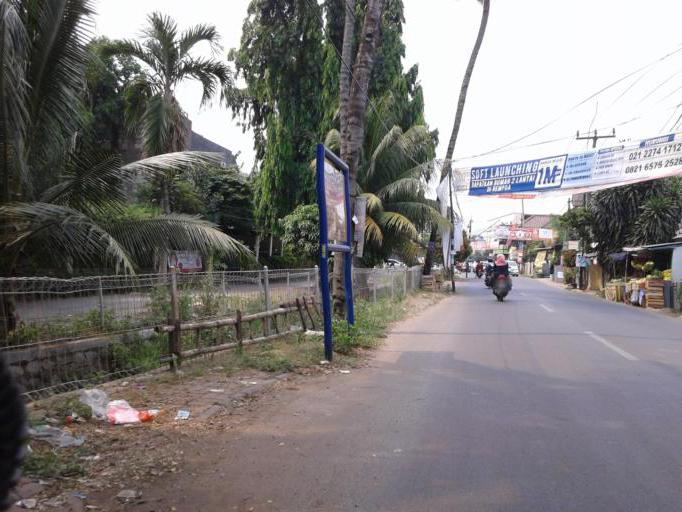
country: ID
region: West Java
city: Pamulang
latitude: -6.3156
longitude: 106.7587
